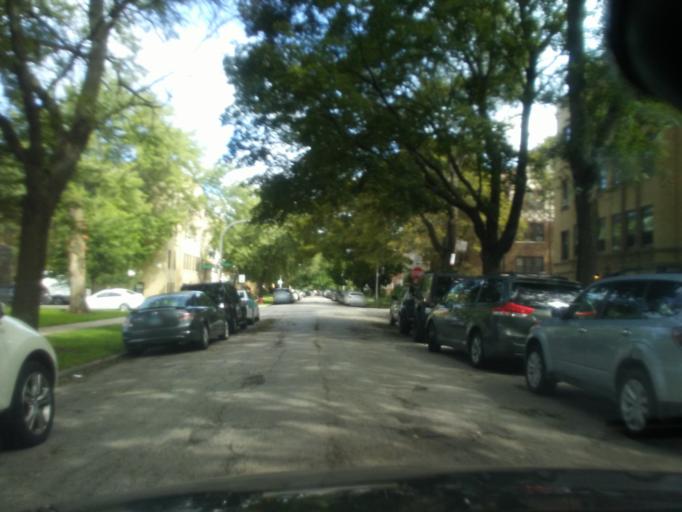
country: US
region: Illinois
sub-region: Cook County
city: Lincolnwood
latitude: 41.9919
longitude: -87.6957
